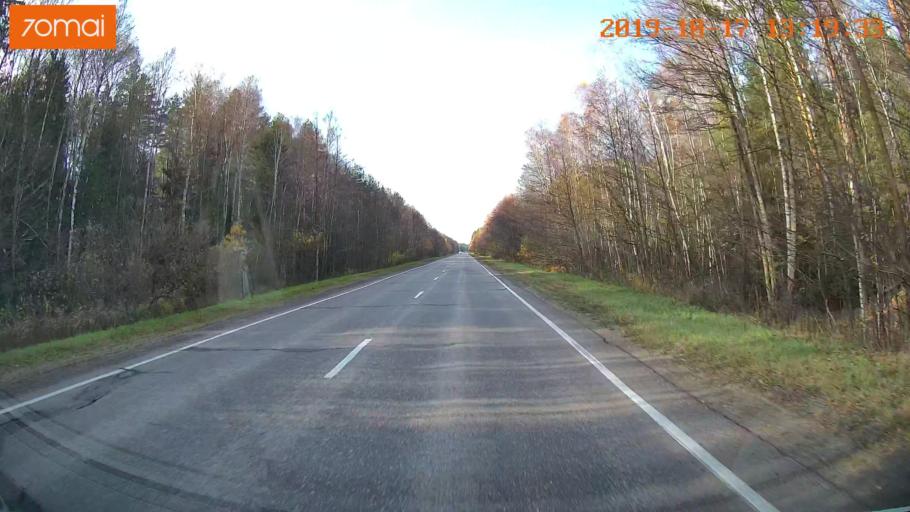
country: RU
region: Rjazan
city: Gus'-Zheleznyy
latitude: 55.0701
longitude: 41.0713
